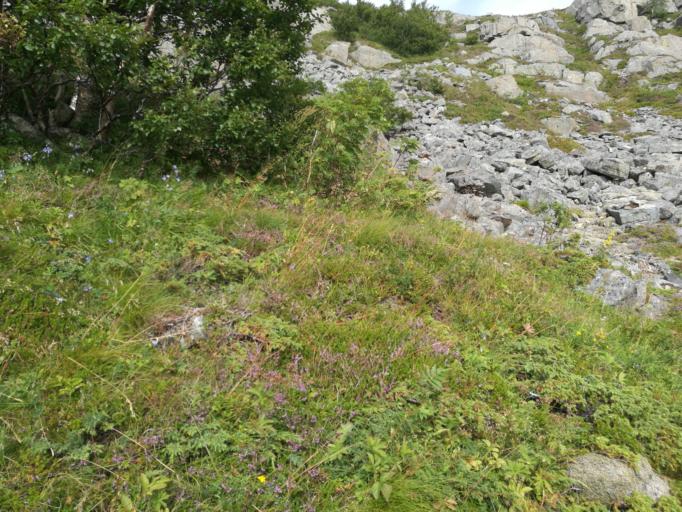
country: NO
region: Nordland
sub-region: Vagan
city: Kabelvag
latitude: 68.1742
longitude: 14.2267
